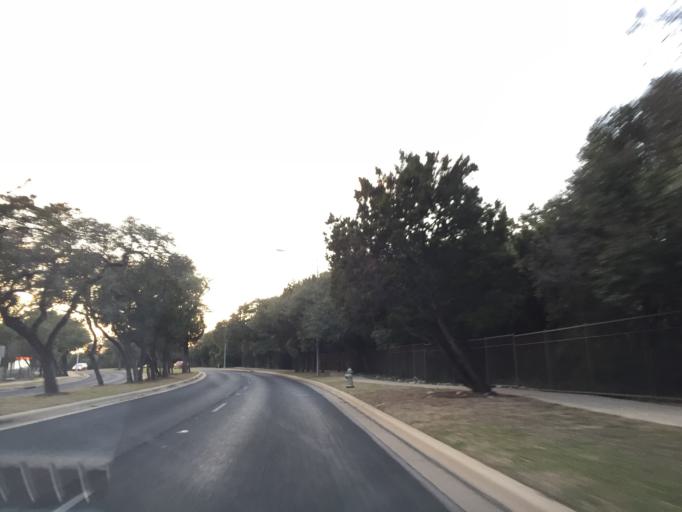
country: US
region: Texas
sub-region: Williamson County
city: Jollyville
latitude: 30.4292
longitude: -97.7494
